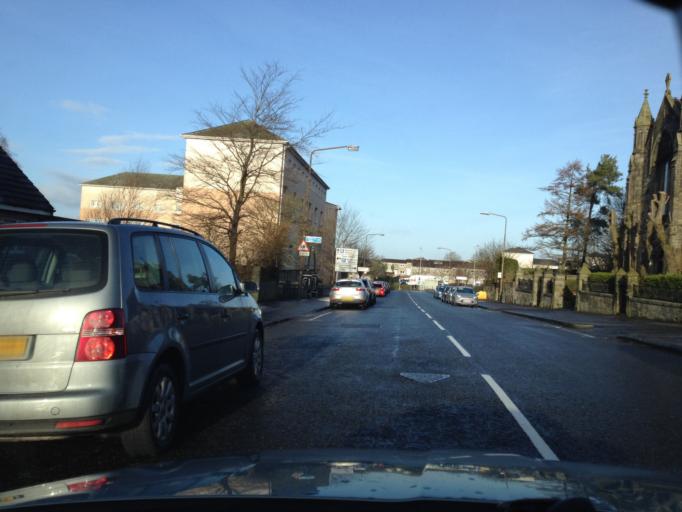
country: GB
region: Scotland
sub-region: West Lothian
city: Bathgate
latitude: 55.9023
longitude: -3.6370
